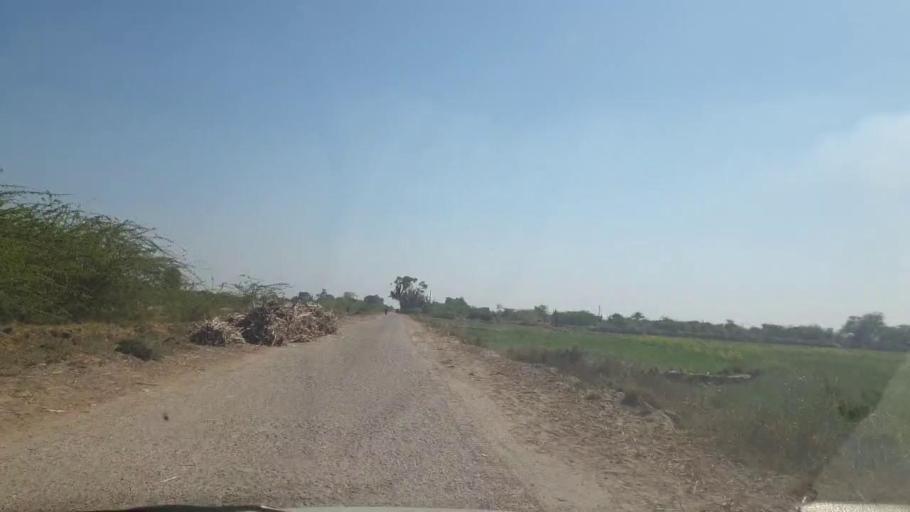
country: PK
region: Sindh
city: Mirpur Khas
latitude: 25.4847
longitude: 69.1702
